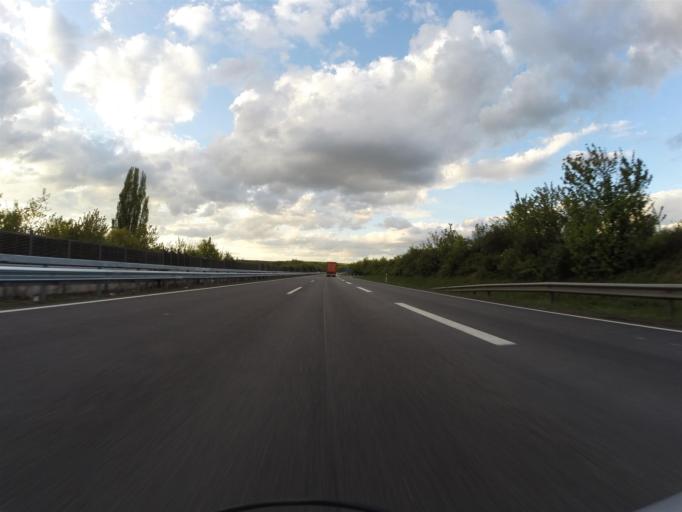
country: DE
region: Rheinland-Pfalz
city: Bischheim
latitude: 49.6654
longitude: 8.0245
